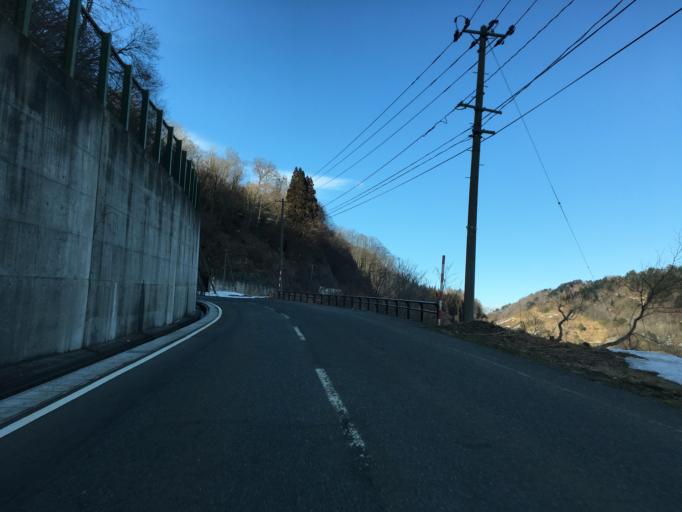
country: JP
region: Yamagata
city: Nagai
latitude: 37.9717
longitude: 139.9164
